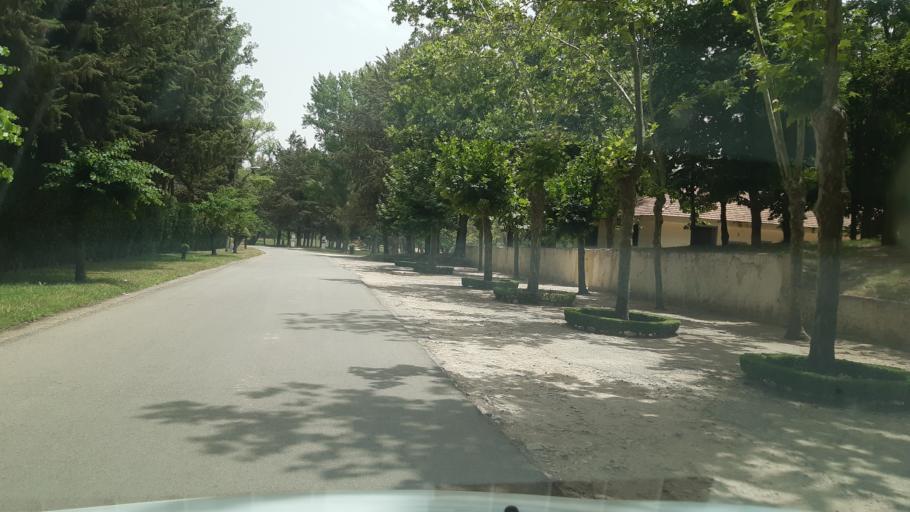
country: MA
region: Meknes-Tafilalet
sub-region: Ifrane
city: Ifrane
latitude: 33.6480
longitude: -5.0334
